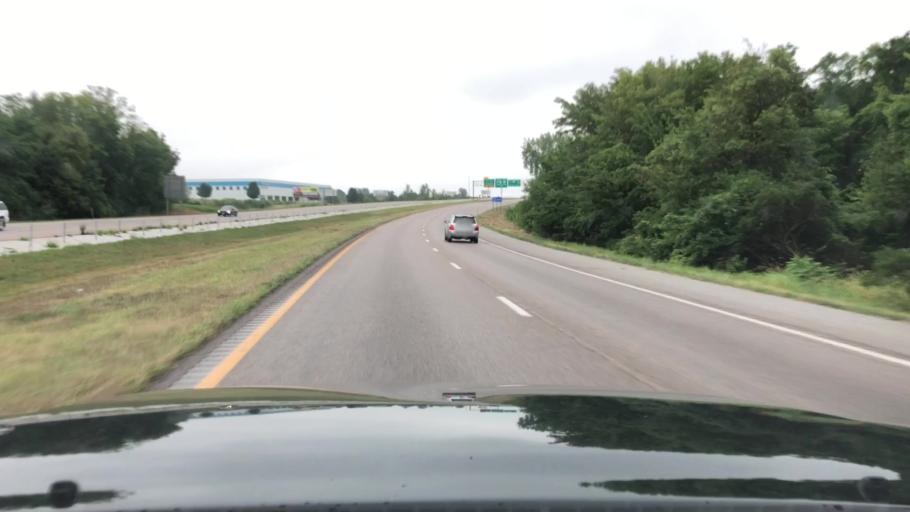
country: US
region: Missouri
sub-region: Saint Charles County
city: Wentzville
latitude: 38.8185
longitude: -90.8451
